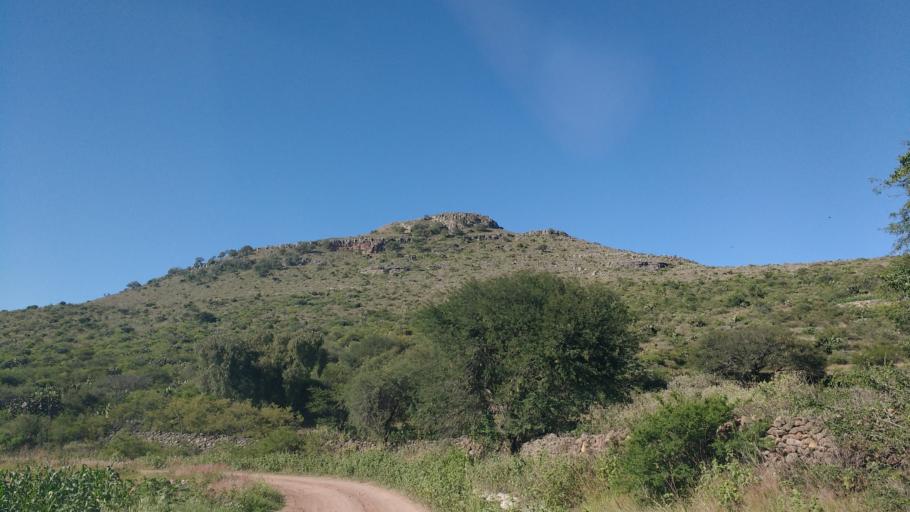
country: MX
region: Hidalgo
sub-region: Tezontepec de Aldama
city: Tenango
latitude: 20.2417
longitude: -99.2783
